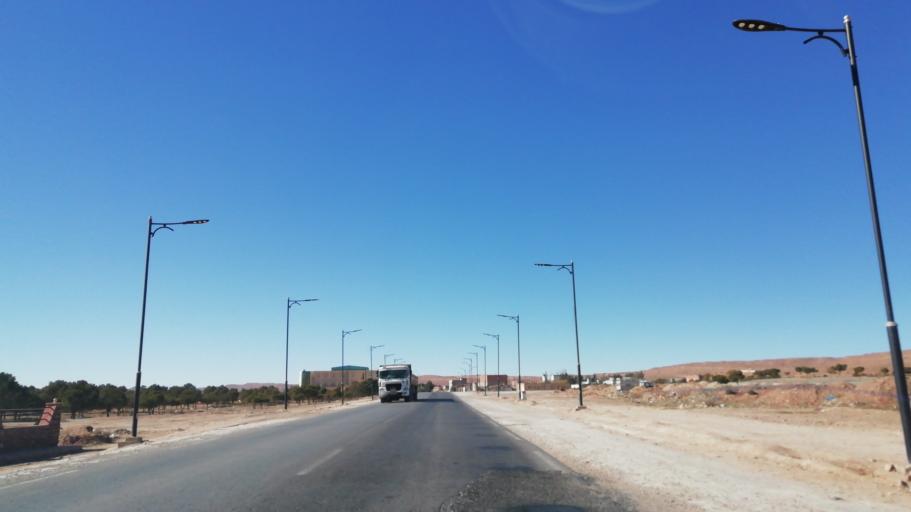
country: DZ
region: El Bayadh
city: El Bayadh
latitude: 33.7289
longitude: 1.5443
